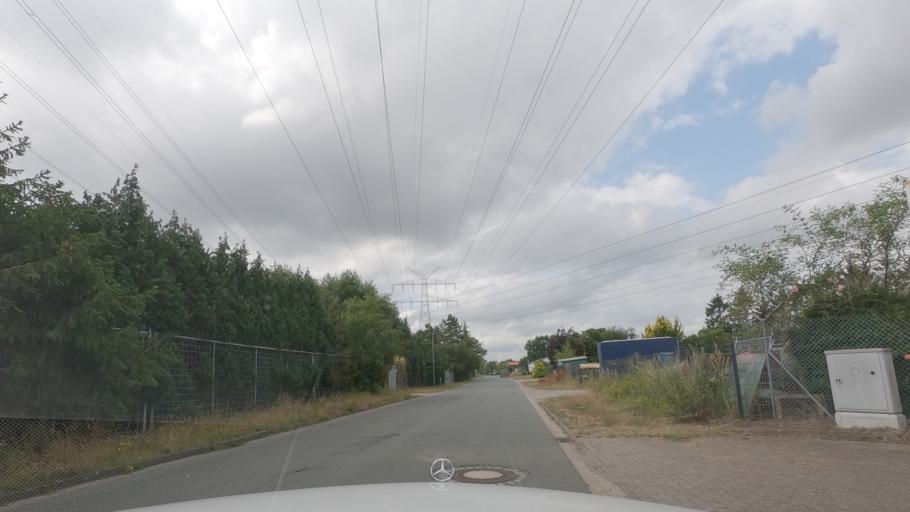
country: DE
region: Lower Saxony
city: Neuenkirchen
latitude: 53.2298
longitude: 8.5396
